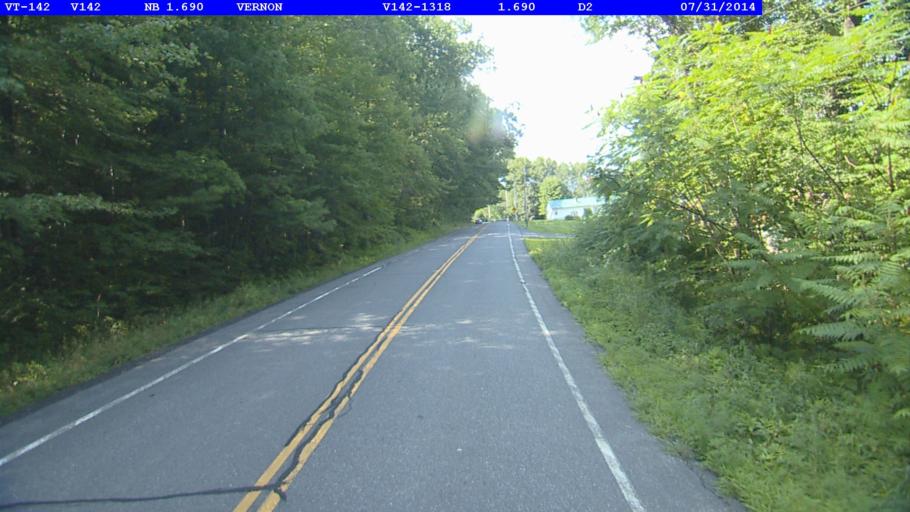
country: US
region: New Hampshire
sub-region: Cheshire County
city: Hinsdale
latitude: 42.7487
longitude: -72.4785
